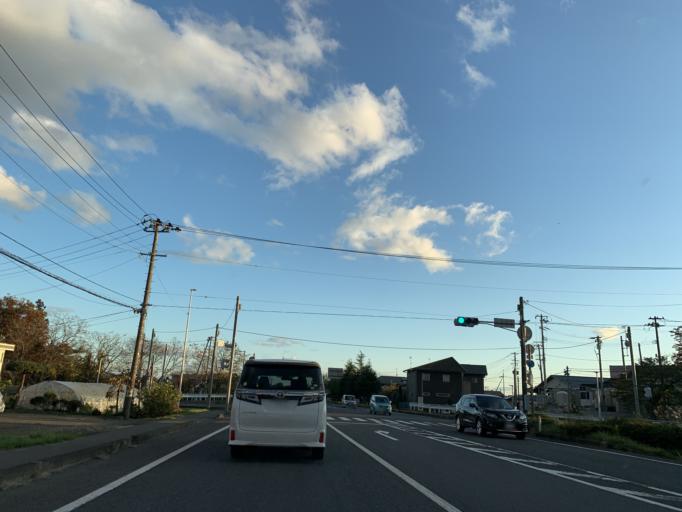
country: JP
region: Iwate
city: Mizusawa
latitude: 39.1968
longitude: 141.1123
